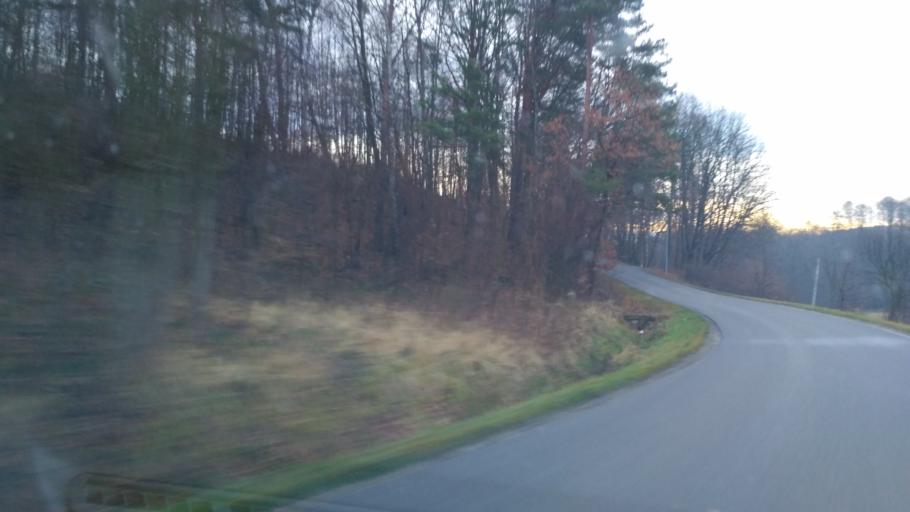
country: PL
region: Subcarpathian Voivodeship
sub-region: Powiat strzyzowski
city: Niebylec
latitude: 49.8588
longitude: 21.8952
